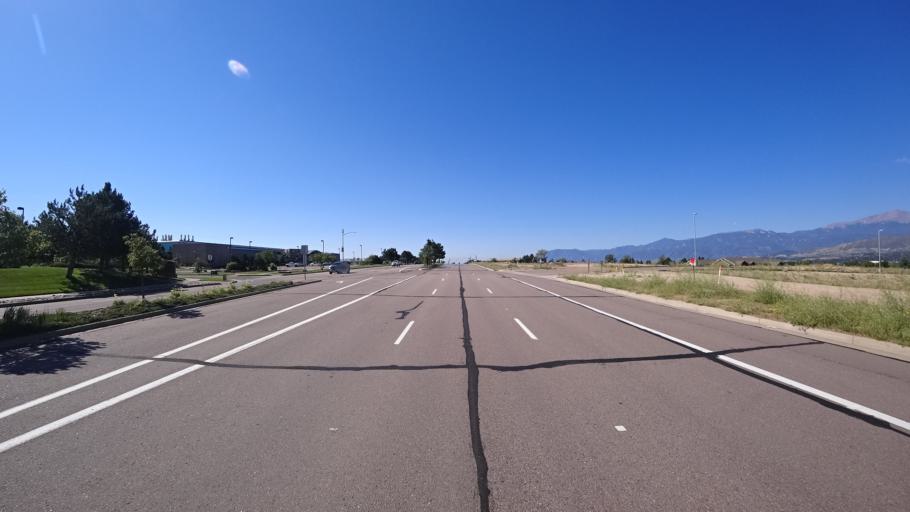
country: US
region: Colorado
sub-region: El Paso County
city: Air Force Academy
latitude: 38.9640
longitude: -104.7848
